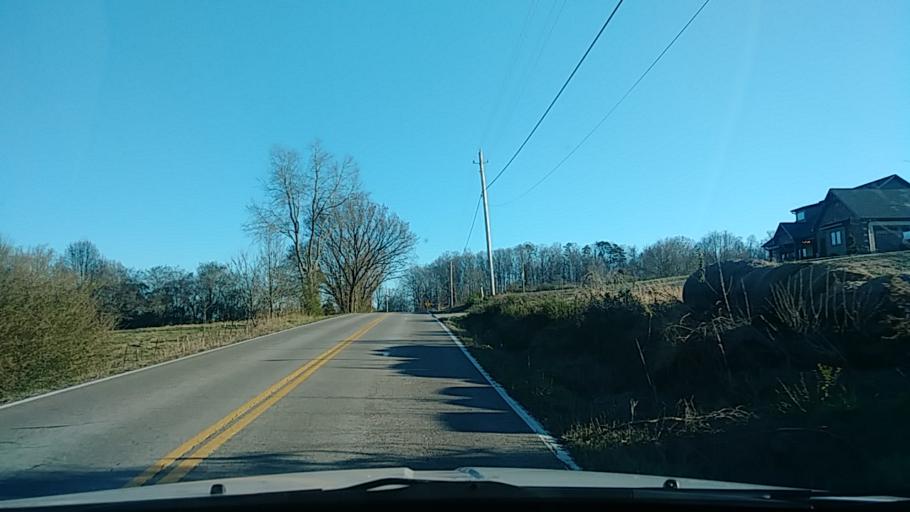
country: US
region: Tennessee
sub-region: Hamblen County
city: Morristown
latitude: 36.2013
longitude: -83.4021
